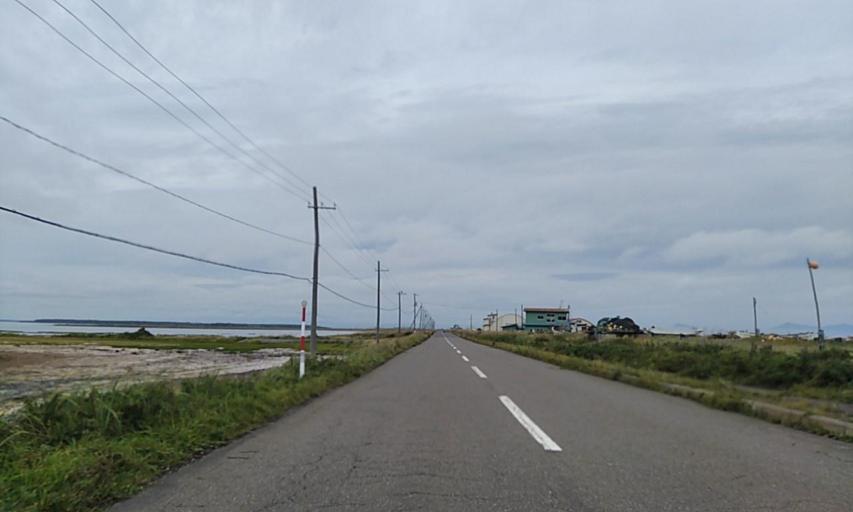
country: JP
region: Hokkaido
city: Shibetsu
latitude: 43.5922
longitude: 145.3326
